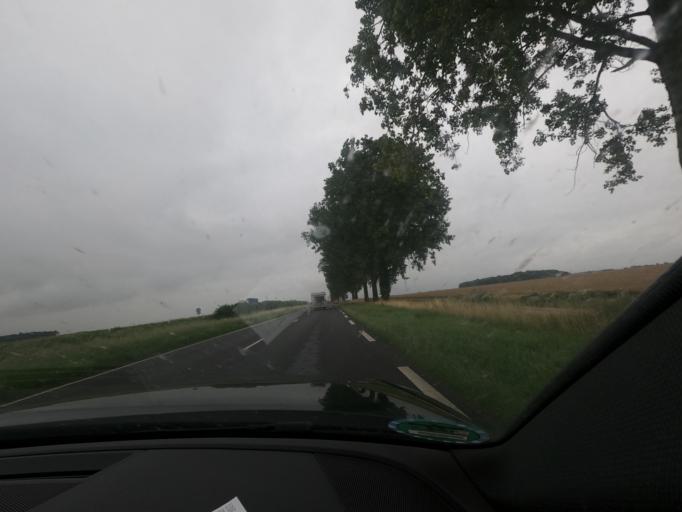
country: FR
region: Picardie
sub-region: Departement de la Somme
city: Rosieres-en-Santerre
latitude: 49.7364
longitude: 2.6974
